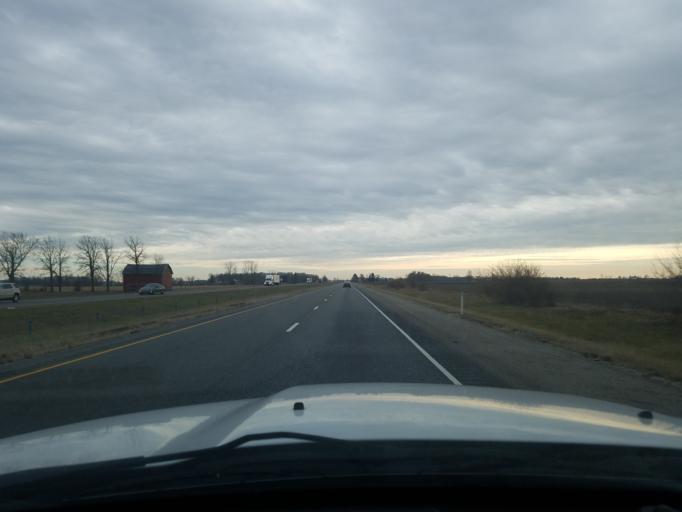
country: US
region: Indiana
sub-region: Grant County
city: Upland
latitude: 40.3972
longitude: -85.5489
